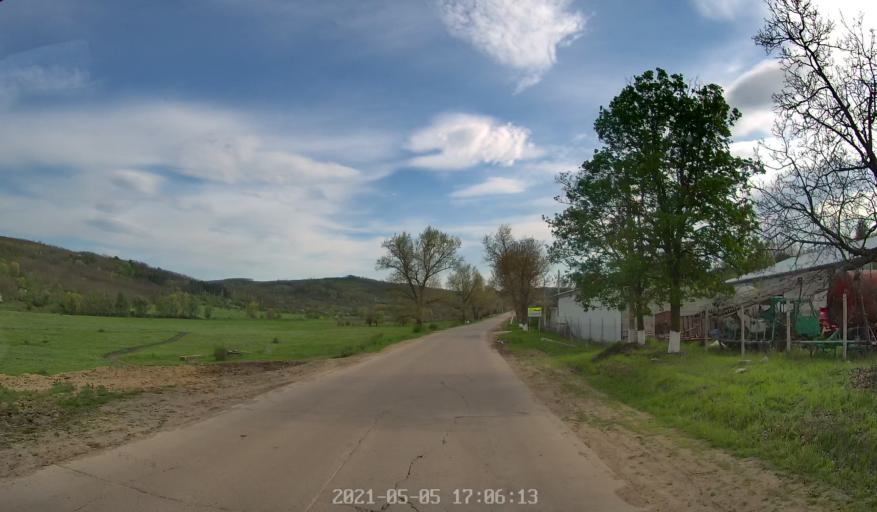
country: MD
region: Chisinau
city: Vadul lui Voda
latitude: 47.0223
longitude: 29.1402
